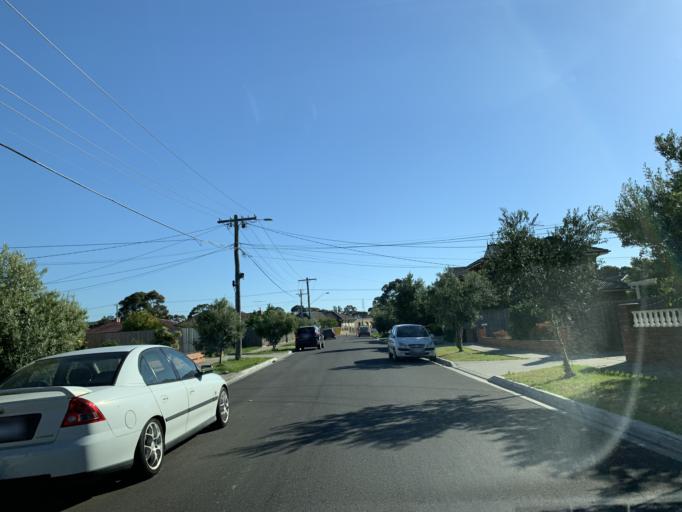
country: AU
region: Victoria
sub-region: Brimbank
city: St Albans
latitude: -37.7567
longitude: 144.8047
